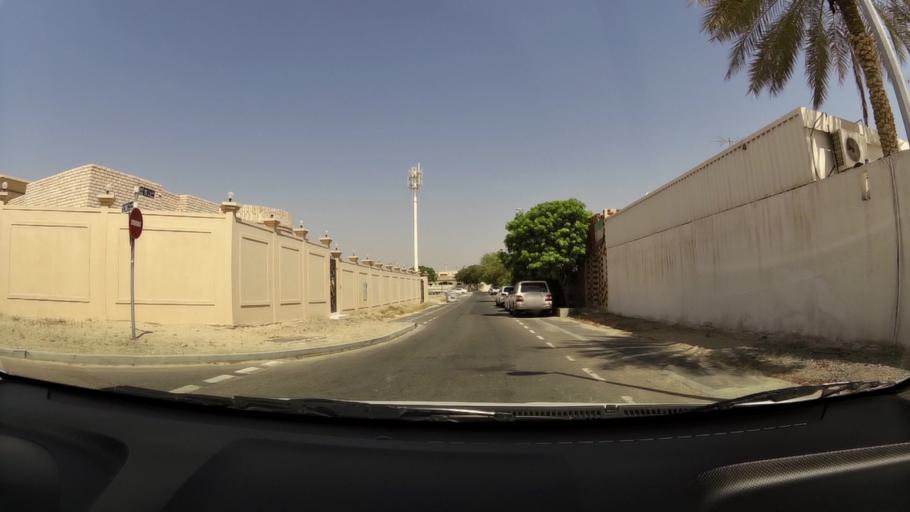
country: AE
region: Ash Shariqah
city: Sharjah
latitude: 25.2729
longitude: 55.3615
